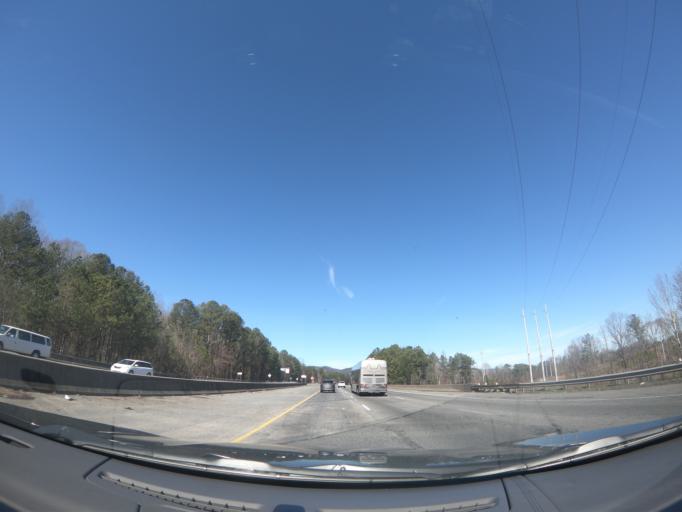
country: US
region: Georgia
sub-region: Whitfield County
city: Dalton
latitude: 34.6671
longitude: -84.9934
